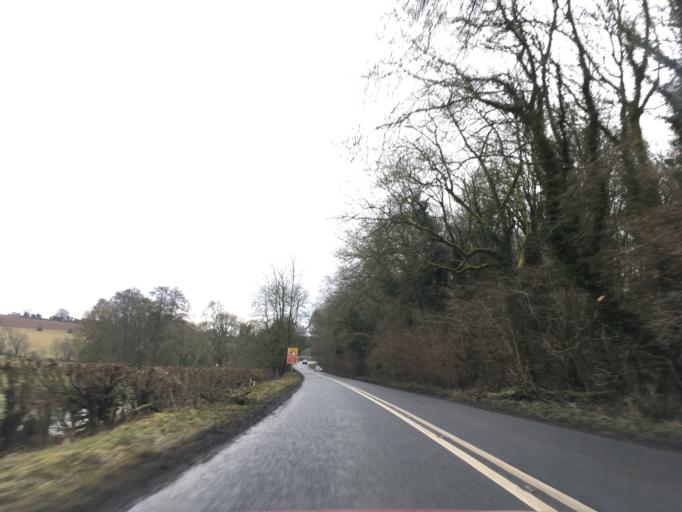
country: GB
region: England
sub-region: Gloucestershire
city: Cirencester
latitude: 51.7620
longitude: -1.9706
